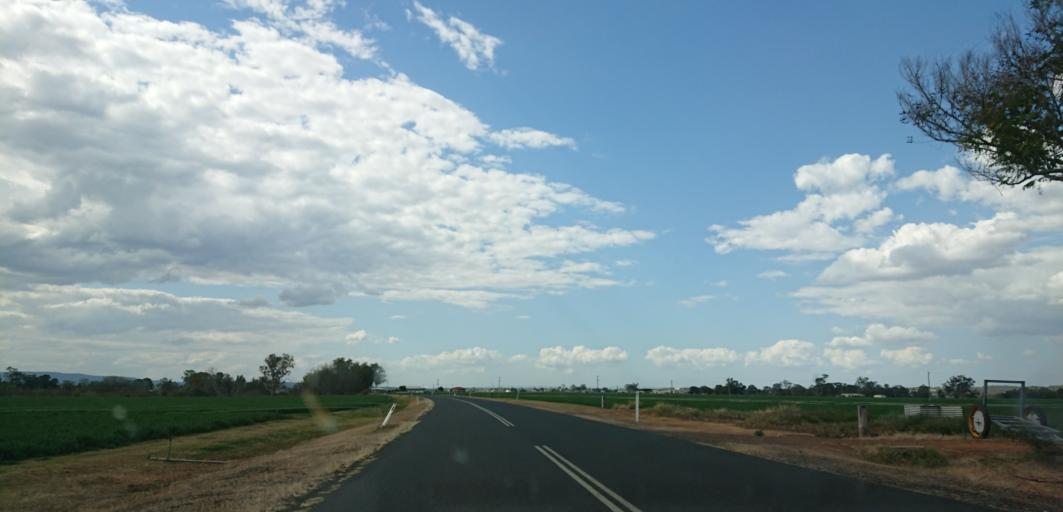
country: AU
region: Queensland
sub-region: Lockyer Valley
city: Gatton
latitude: -27.5968
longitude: 152.2232
